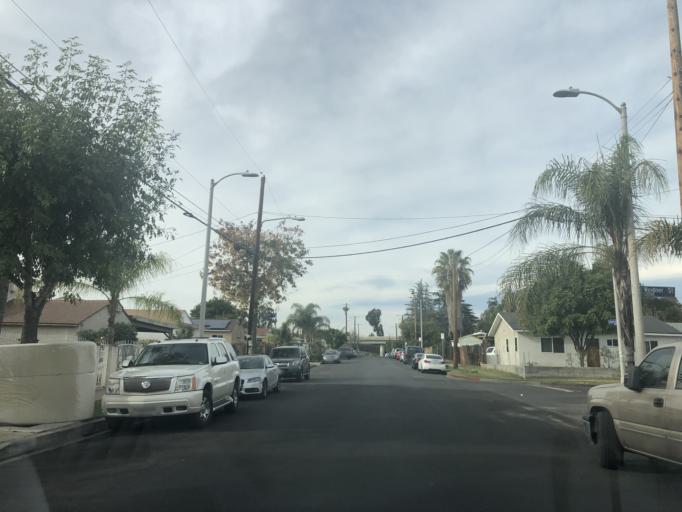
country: US
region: California
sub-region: Los Angeles County
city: San Fernando
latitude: 34.2691
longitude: -118.4283
